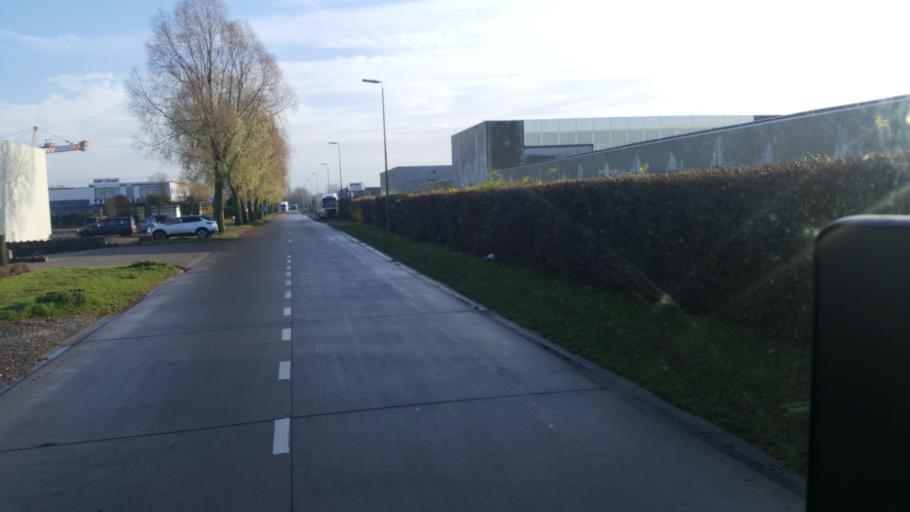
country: BE
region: Flanders
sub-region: Provincie Limburg
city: Maasmechelen
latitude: 50.9436
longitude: 5.7033
